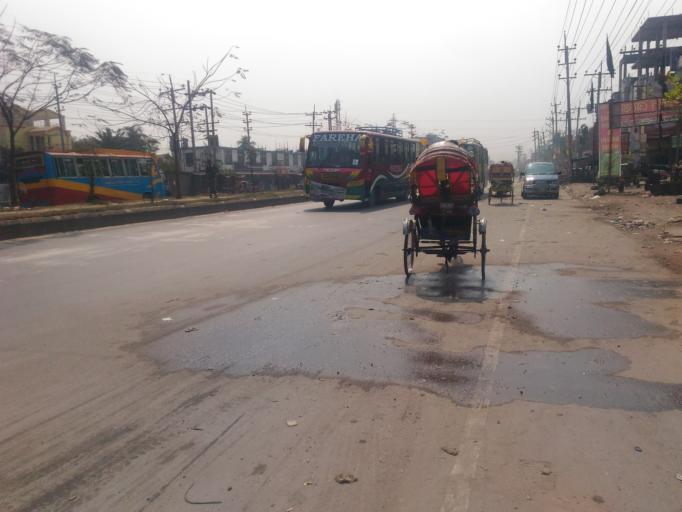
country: BD
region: Dhaka
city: Tungi
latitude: 24.0006
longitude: 90.3827
